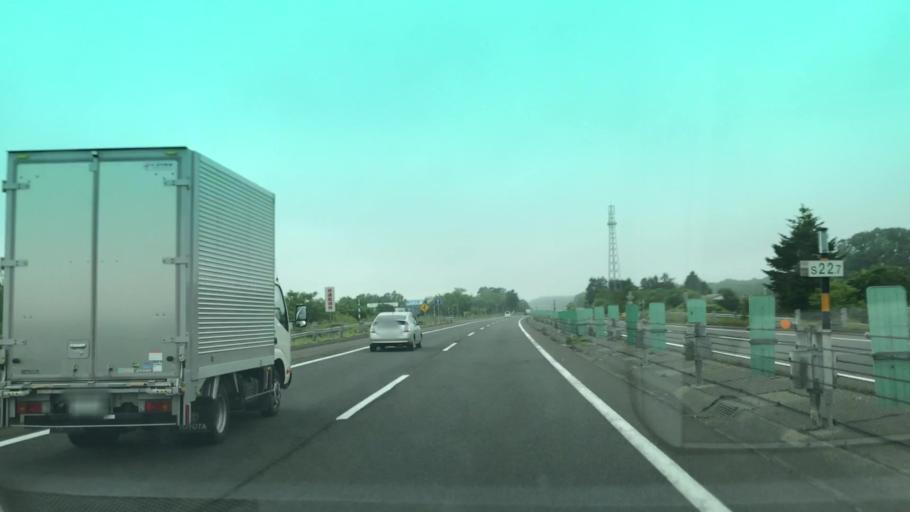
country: JP
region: Hokkaido
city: Kitahiroshima
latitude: 42.9030
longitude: 141.5507
